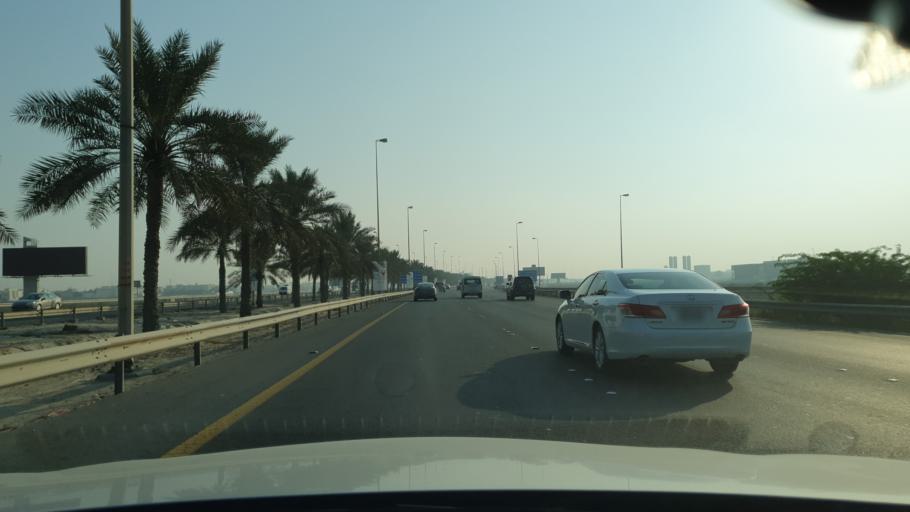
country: BH
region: Northern
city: Madinat `Isa
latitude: 26.1927
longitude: 50.5186
